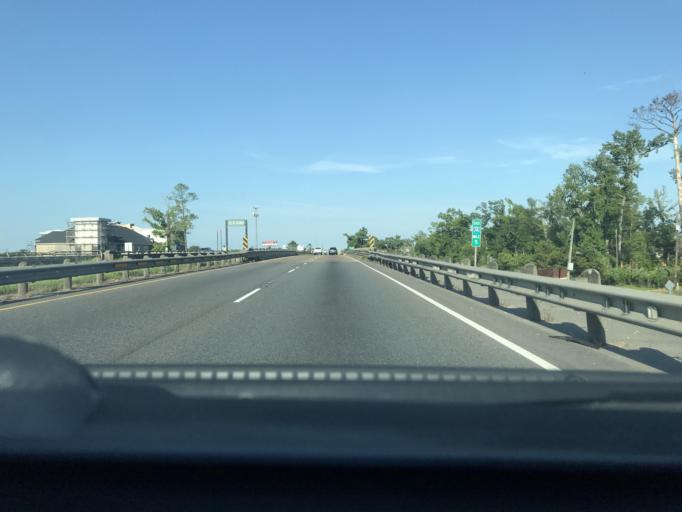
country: US
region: Louisiana
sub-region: Calcasieu Parish
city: Prien
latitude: 30.1968
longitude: -93.2417
